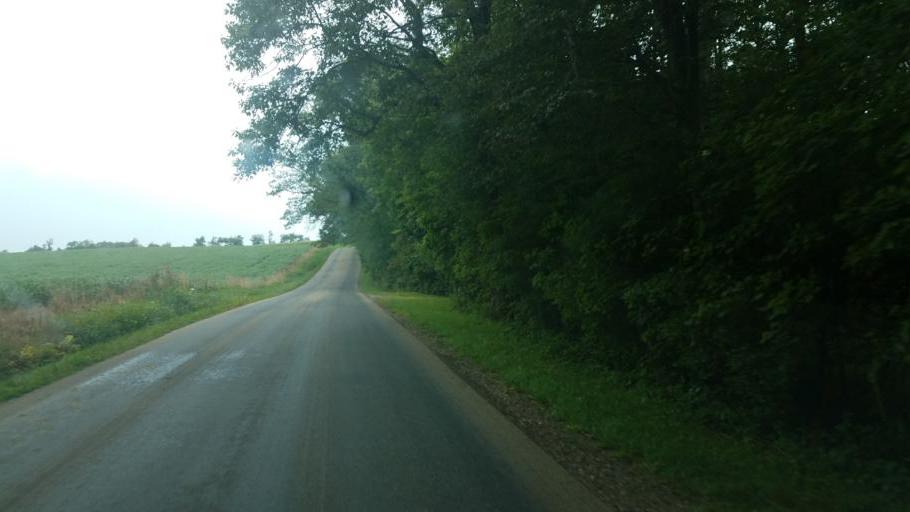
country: US
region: Ohio
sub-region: Knox County
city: Danville
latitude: 40.5206
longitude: -82.3819
